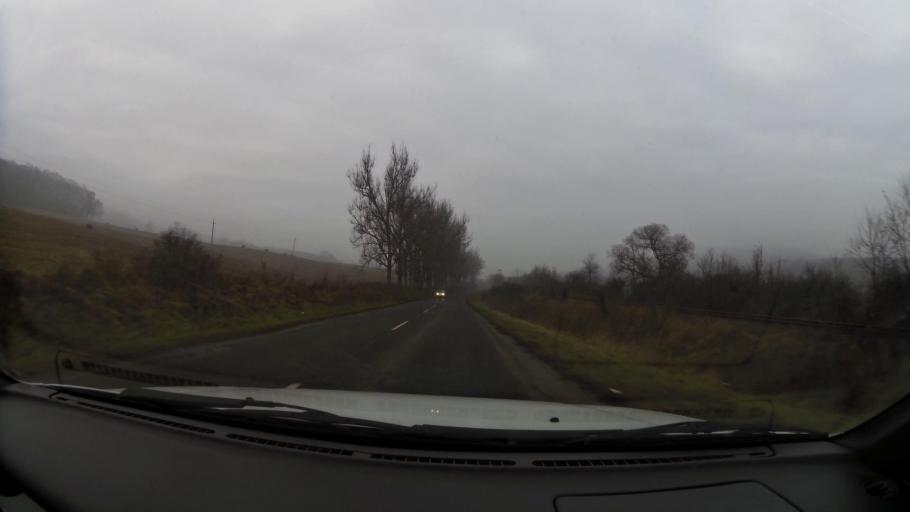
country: HU
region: Borsod-Abauj-Zemplen
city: Rudabanya
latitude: 48.3465
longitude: 20.6424
